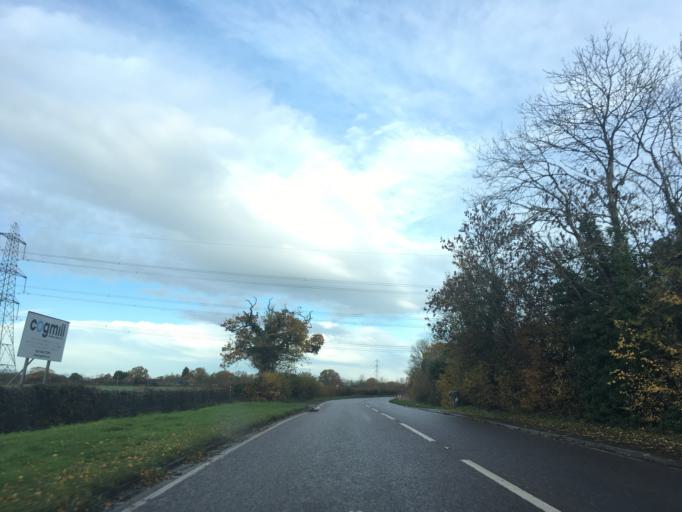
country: GB
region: England
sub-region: South Gloucestershire
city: Winterbourne
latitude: 51.5439
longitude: -2.4833
